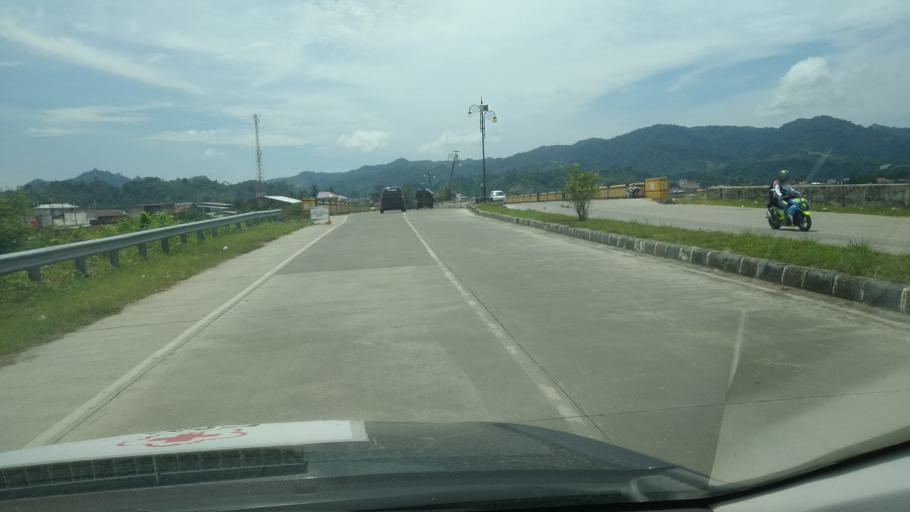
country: ID
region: Sulawesi Barat
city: Mamuju
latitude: -2.6805
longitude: 118.8742
